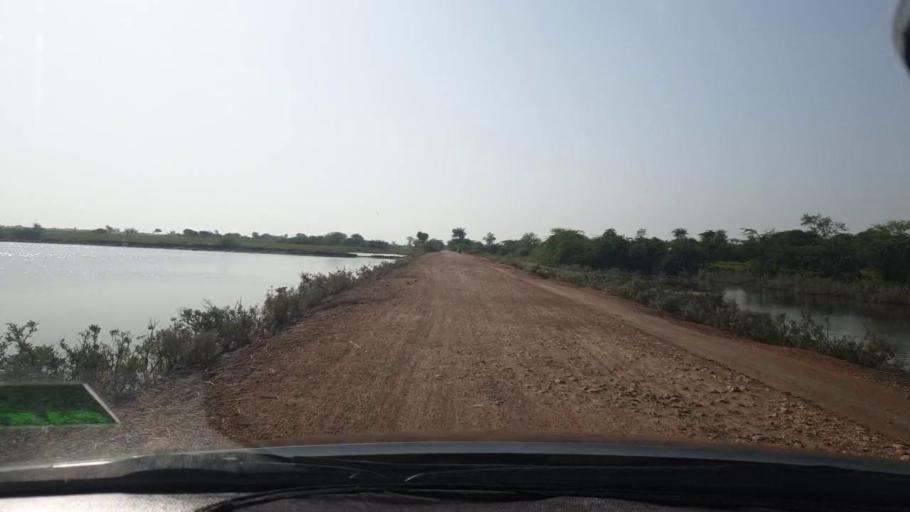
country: PK
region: Sindh
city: Tando Bago
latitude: 24.7226
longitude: 68.9582
